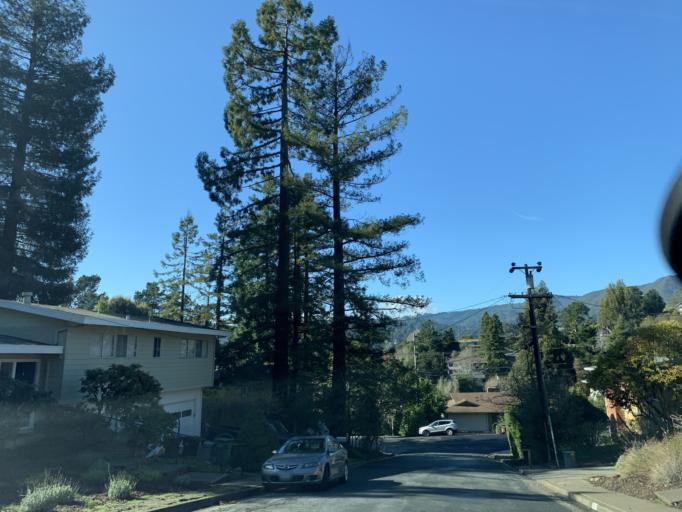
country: US
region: California
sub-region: Marin County
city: Strawberry
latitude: 37.8993
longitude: -122.5205
